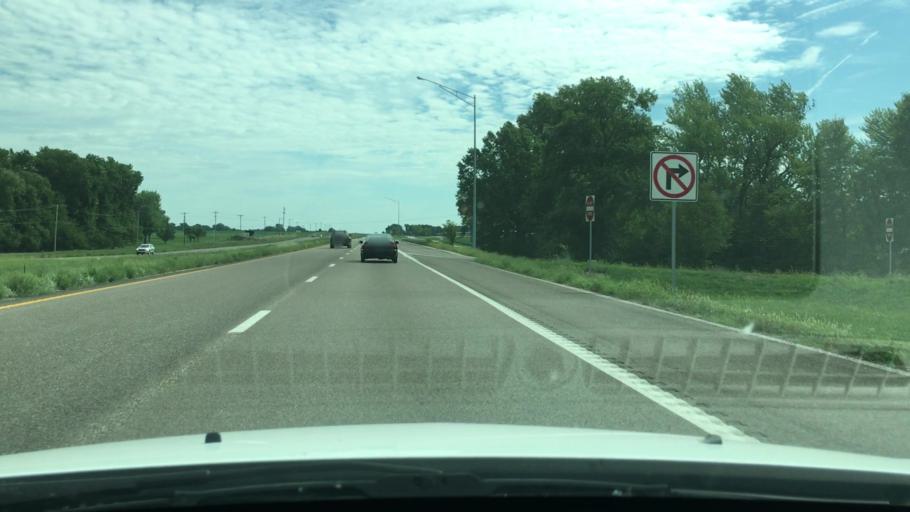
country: US
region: Missouri
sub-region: Callaway County
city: Fulton
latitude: 38.9587
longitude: -91.9293
